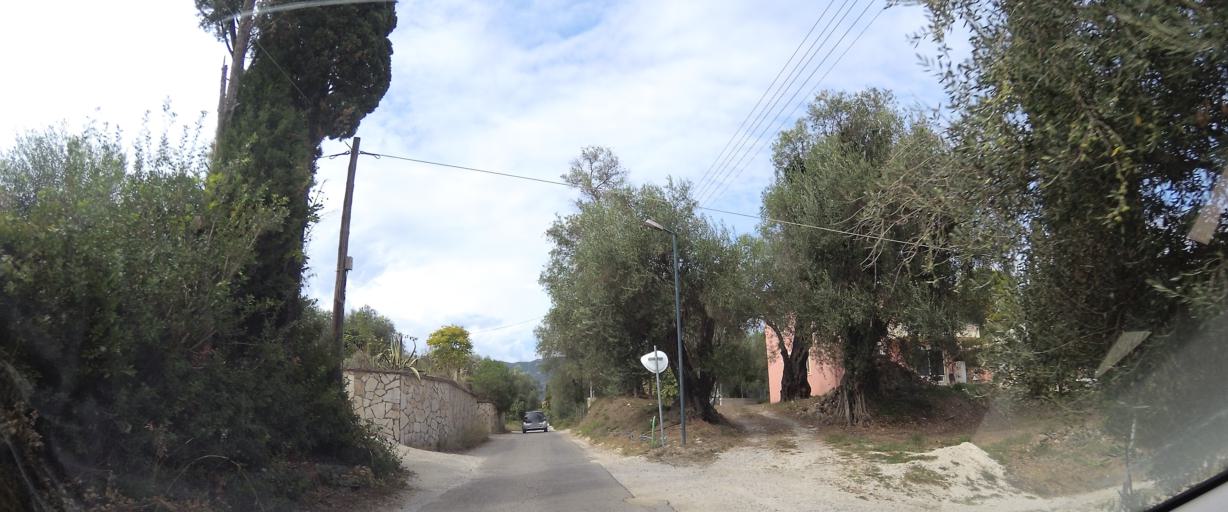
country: GR
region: Ionian Islands
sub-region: Nomos Kerkyras
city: Kontokali
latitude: 39.6924
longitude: 19.8133
